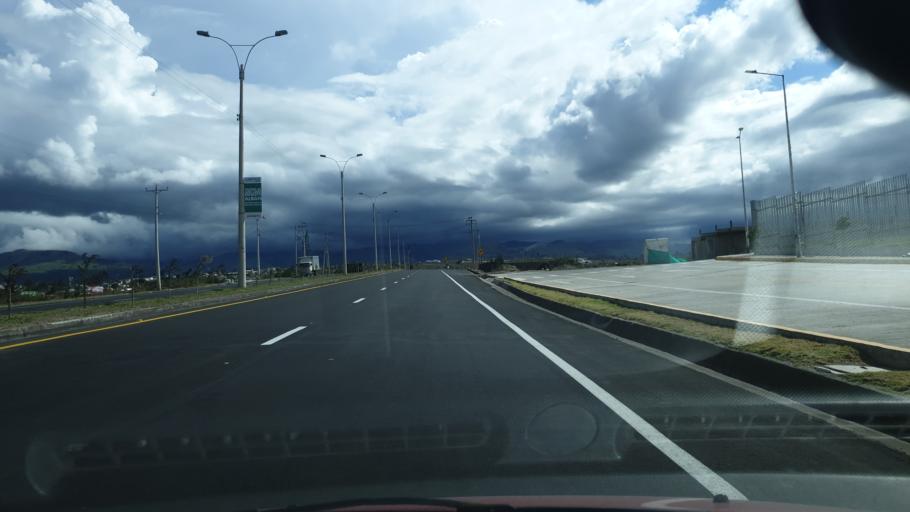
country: EC
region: Tungurahua
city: Ambato
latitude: -1.3019
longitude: -78.6350
